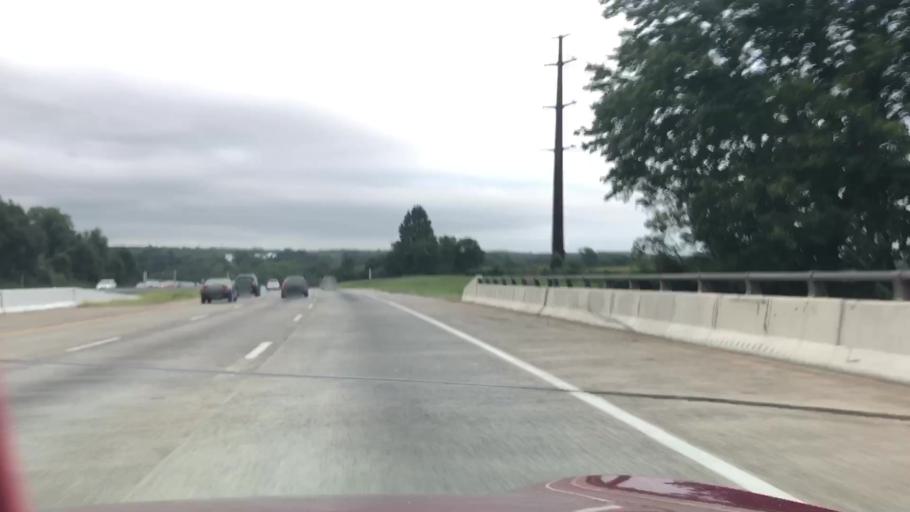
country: US
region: Maryland
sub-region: Cecil County
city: Elkton
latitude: 39.6423
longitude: -75.8746
